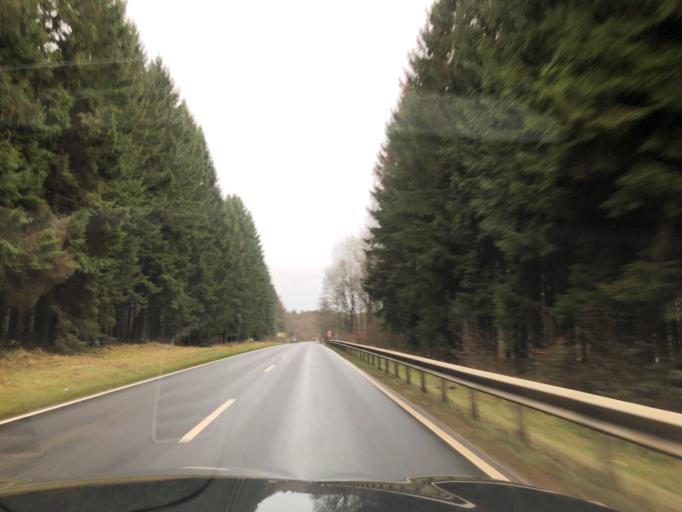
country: DE
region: Rheinland-Pfalz
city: Windhagen
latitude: 50.6349
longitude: 7.3057
